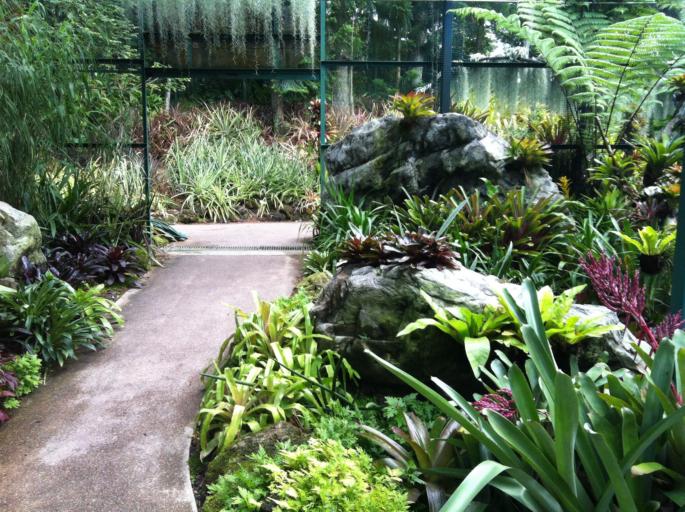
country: SG
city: Singapore
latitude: 1.3132
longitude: 103.8145
